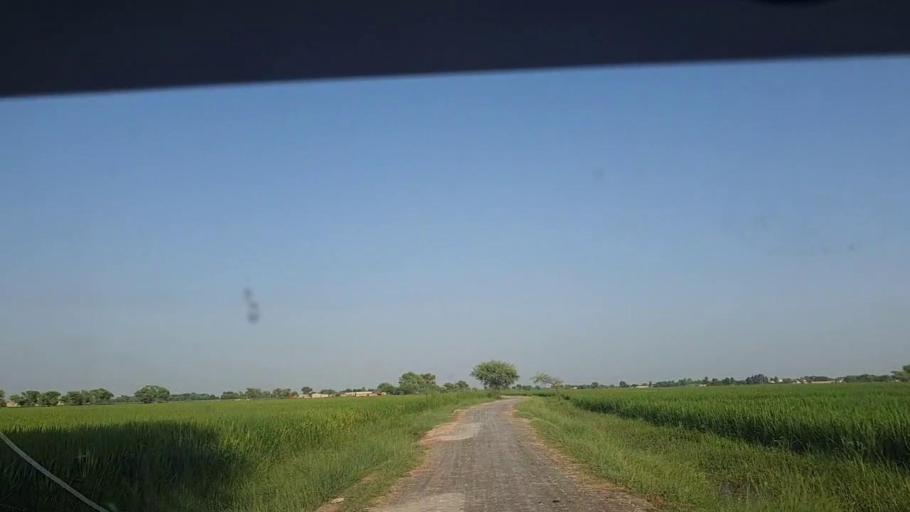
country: PK
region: Sindh
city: Tangwani
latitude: 28.2709
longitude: 69.0034
